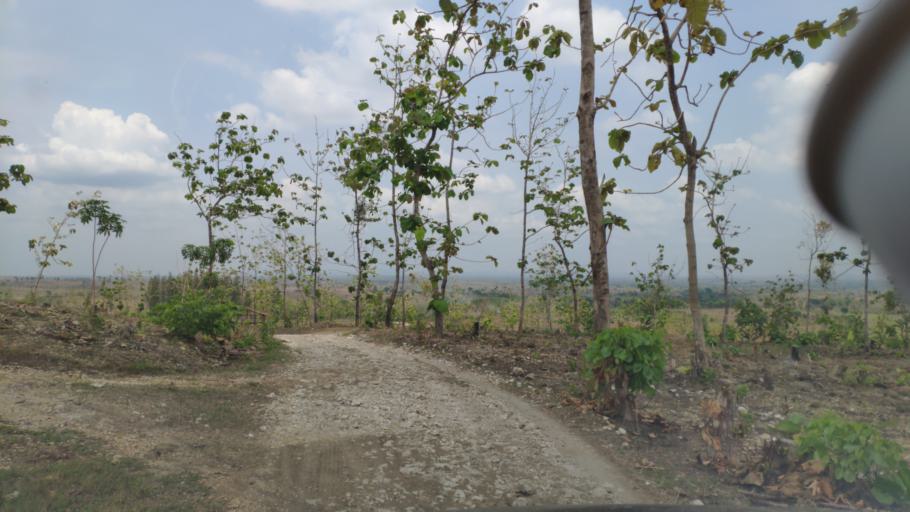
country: ID
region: Central Java
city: Gumiring
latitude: -7.0510
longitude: 111.4003
